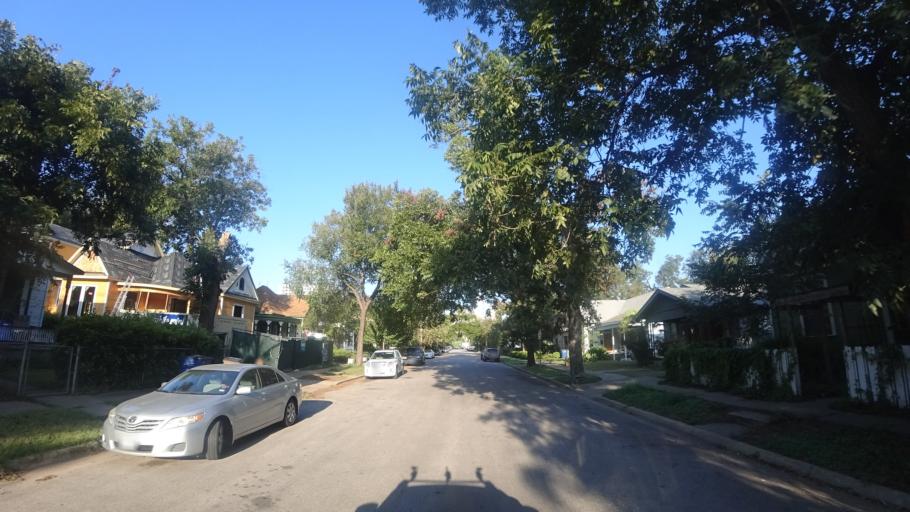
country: US
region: Texas
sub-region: Travis County
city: Austin
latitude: 30.2593
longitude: -97.7340
